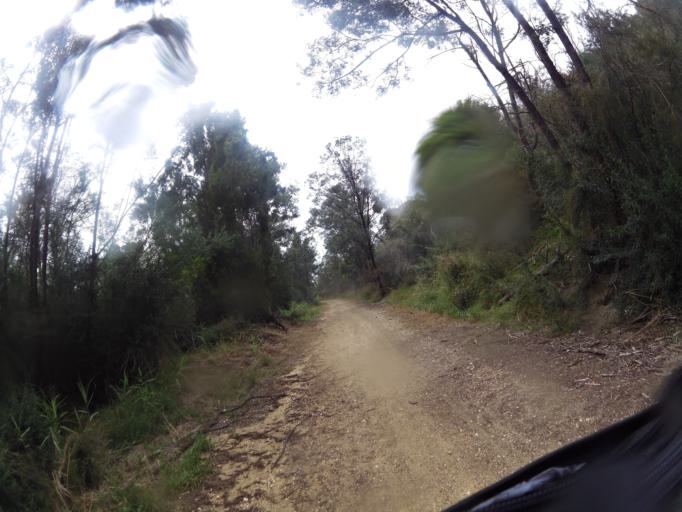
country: AU
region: Victoria
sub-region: East Gippsland
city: Bairnsdale
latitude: -37.7415
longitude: 147.8103
